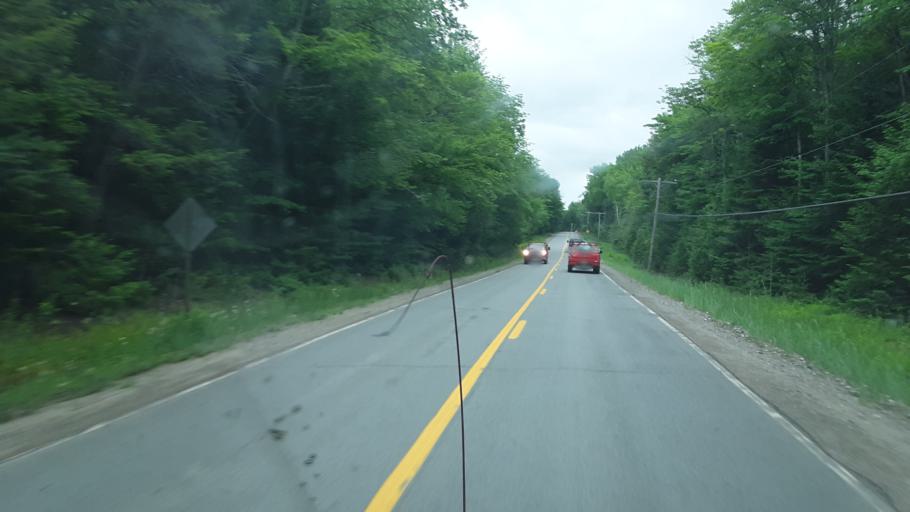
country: US
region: Maine
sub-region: Penobscot County
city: Millinocket
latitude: 45.6798
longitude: -68.7443
